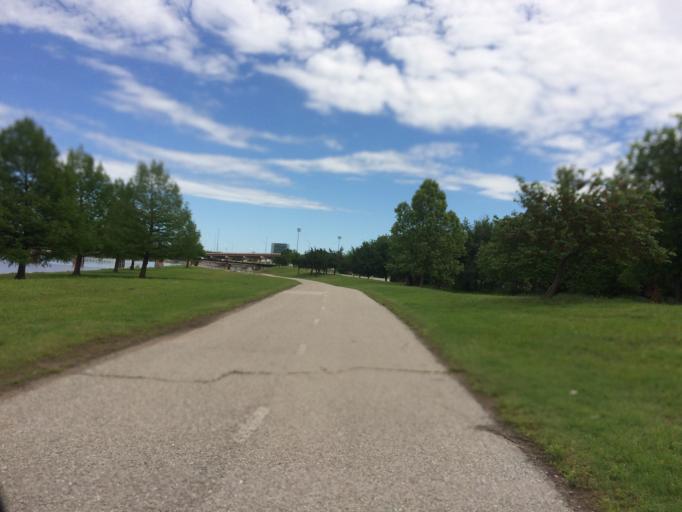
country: US
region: Oklahoma
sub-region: Oklahoma County
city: Oklahoma City
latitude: 35.4536
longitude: -97.5064
